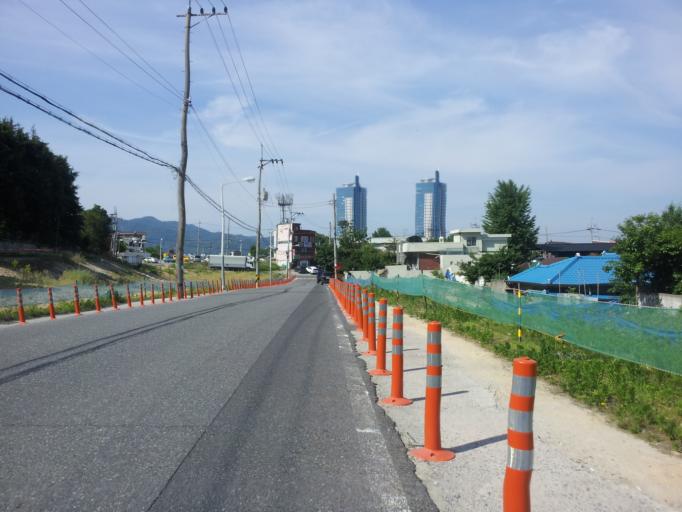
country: KR
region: Daejeon
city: Daejeon
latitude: 36.3370
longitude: 127.4434
